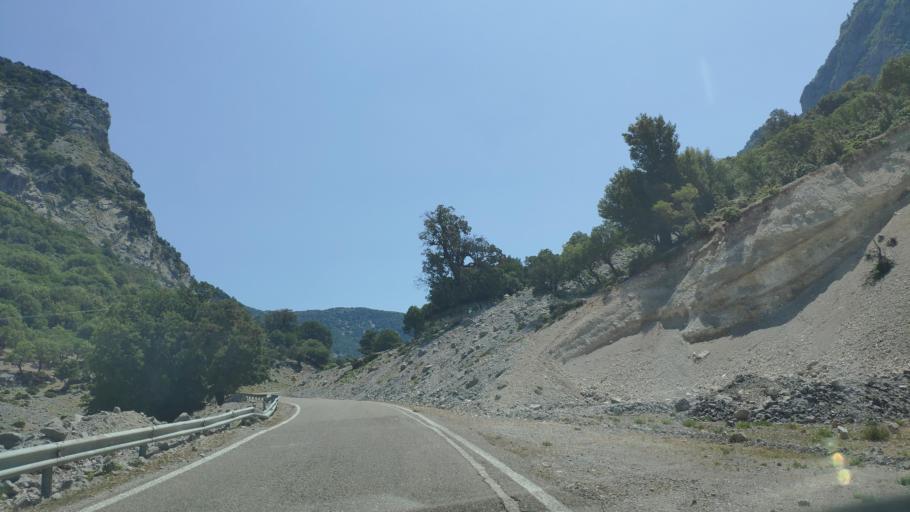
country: GR
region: West Greece
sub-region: Nomos Aitolias kai Akarnanias
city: Krikellos
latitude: 39.0202
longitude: 21.3373
